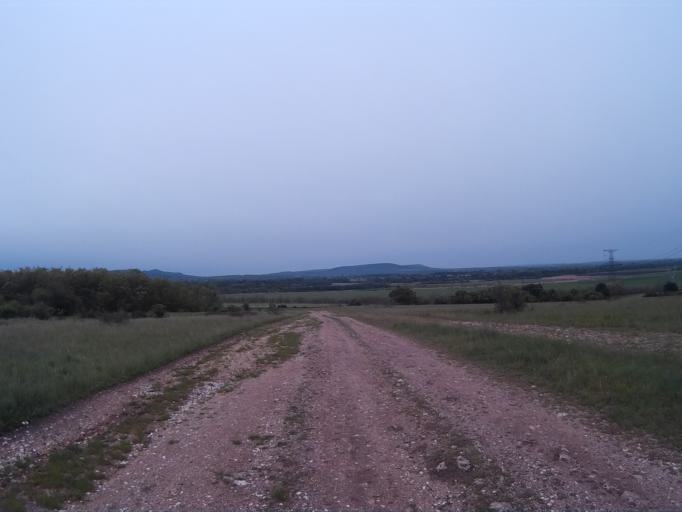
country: HU
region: Veszprem
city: Sumeg
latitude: 46.9611
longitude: 17.2895
